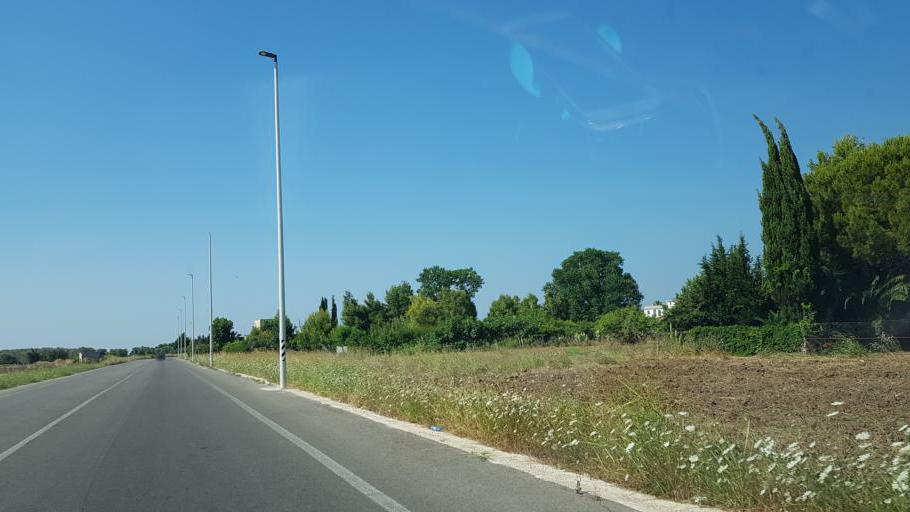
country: IT
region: Apulia
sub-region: Provincia di Lecce
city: Salice Salentino
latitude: 40.3785
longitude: 17.9696
